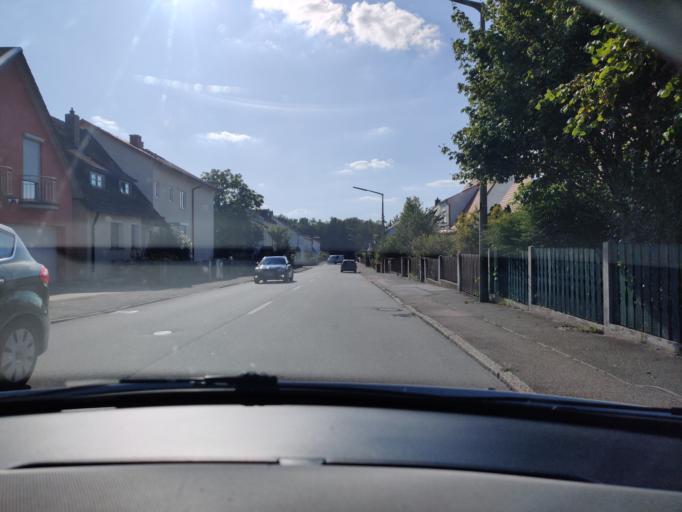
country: DE
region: Bavaria
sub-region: Upper Palatinate
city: Schwandorf in Bayern
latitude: 49.3282
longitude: 12.1193
